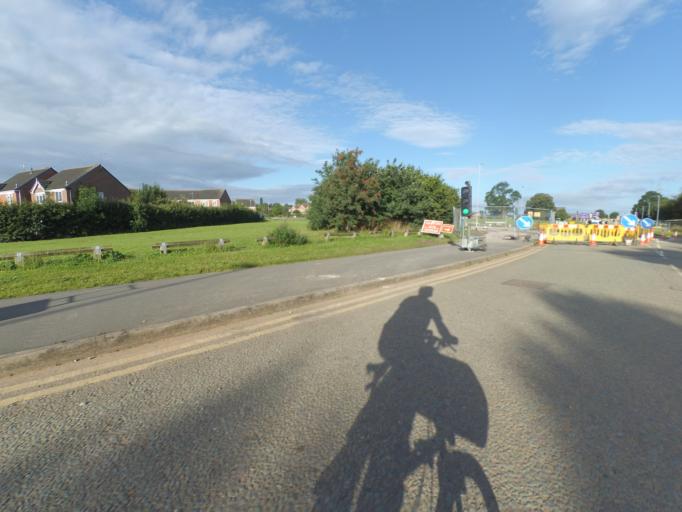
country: GB
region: England
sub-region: Staffordshire
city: Stafford
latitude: 52.8060
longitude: -2.1325
